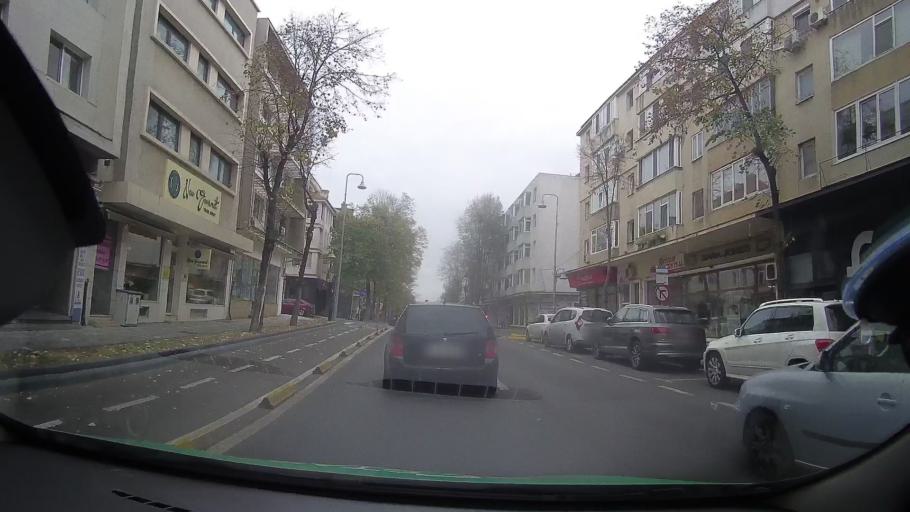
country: RO
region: Constanta
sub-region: Municipiul Constanta
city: Constanta
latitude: 44.1798
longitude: 28.6506
